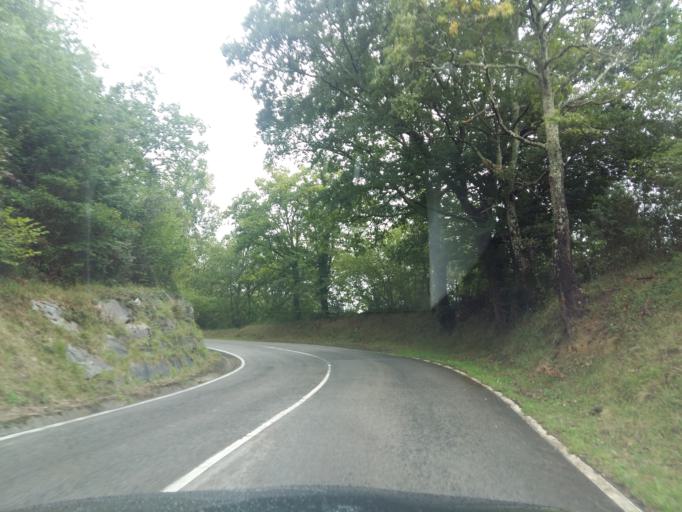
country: ES
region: Basque Country
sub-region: Bizkaia
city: Lanestosa
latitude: 43.1862
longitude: -3.5150
